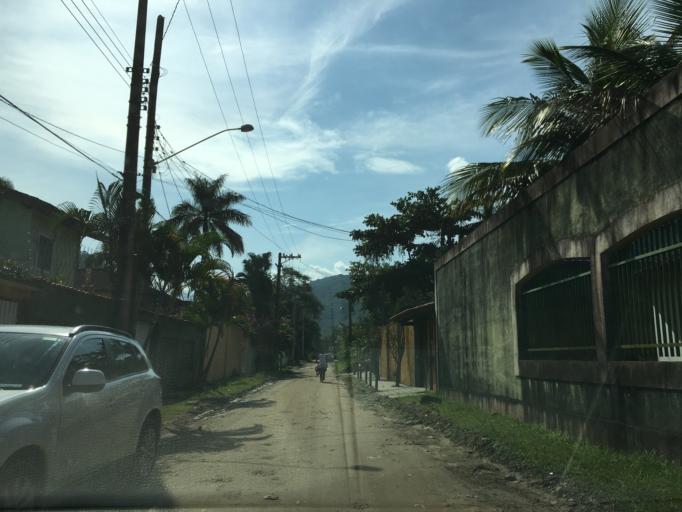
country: BR
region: Sao Paulo
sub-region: Sao Sebastiao
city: Sao Sebastiao
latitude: -23.7608
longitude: -45.7247
